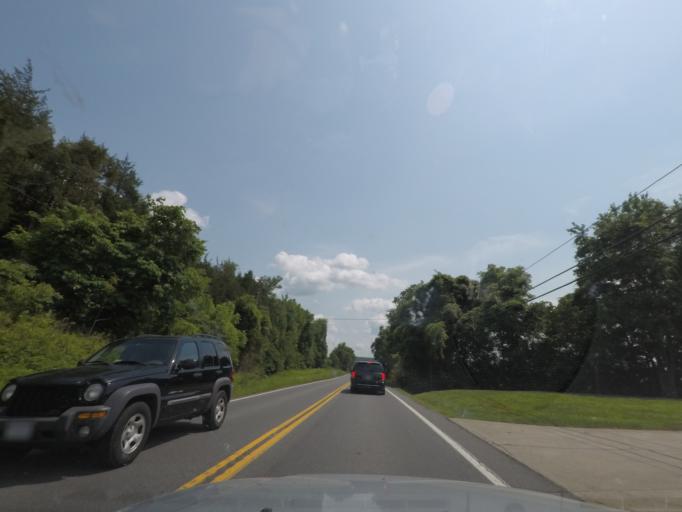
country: US
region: Virginia
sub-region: Orange County
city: Orange
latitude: 38.2913
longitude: -78.1388
